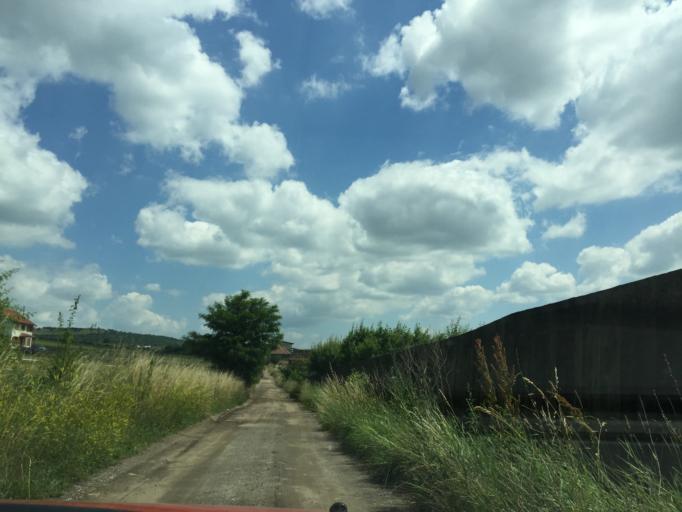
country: RO
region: Cluj
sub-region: Comuna Baciu
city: Baciu
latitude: 46.7910
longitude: 23.5574
